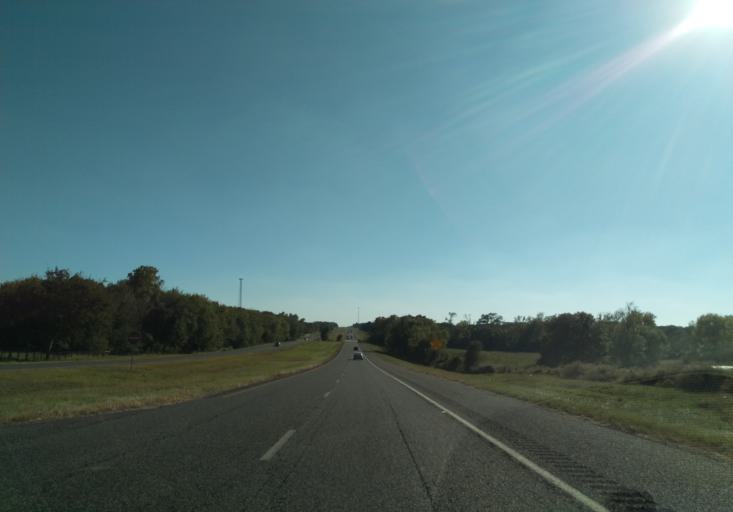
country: US
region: Texas
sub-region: Waller County
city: Hempstead
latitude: 30.1910
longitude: -96.0625
